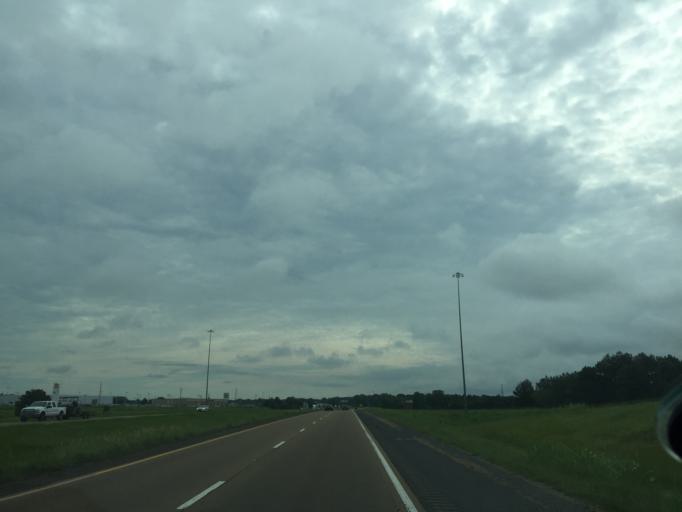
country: US
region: Mississippi
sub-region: Rankin County
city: Brandon
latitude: 32.2778
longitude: -90.0357
